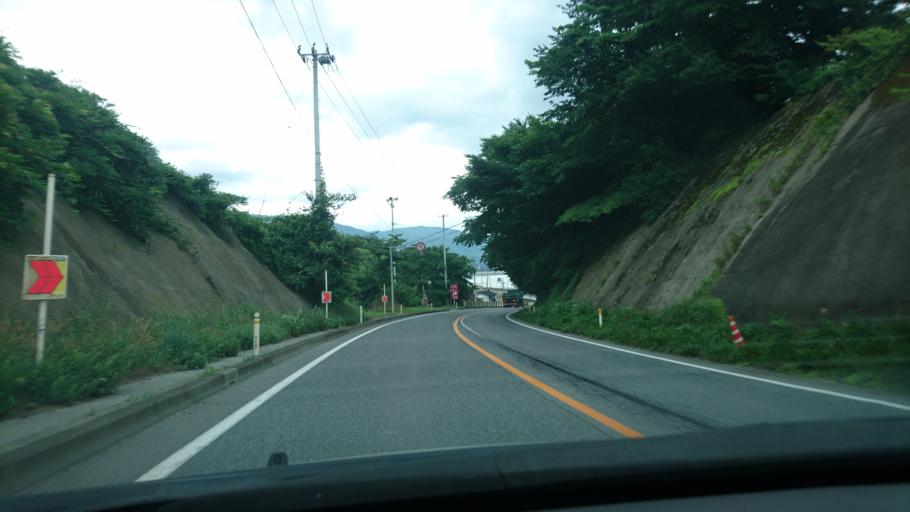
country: JP
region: Iwate
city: Ofunato
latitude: 38.9951
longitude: 141.6188
